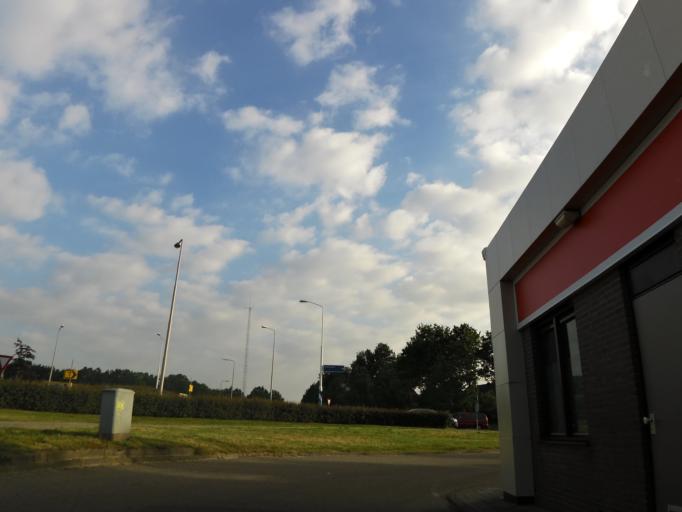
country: NL
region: Limburg
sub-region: Gemeente Onderbanken
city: Schinveld
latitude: 50.9652
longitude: 5.9729
